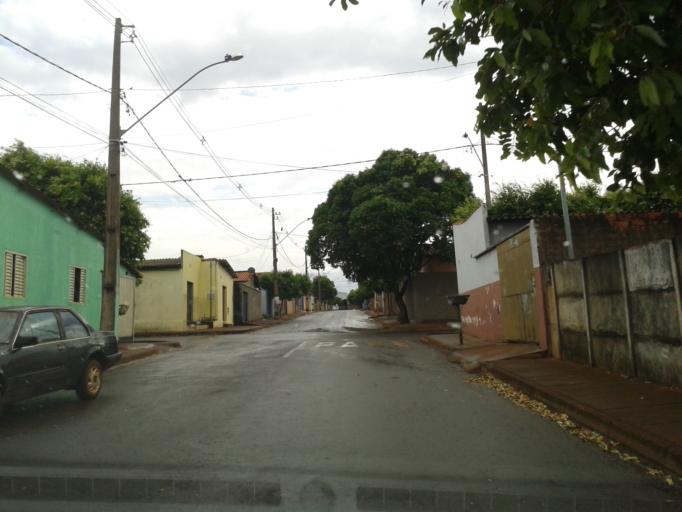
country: BR
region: Minas Gerais
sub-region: Centralina
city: Centralina
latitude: -18.7310
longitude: -49.1996
